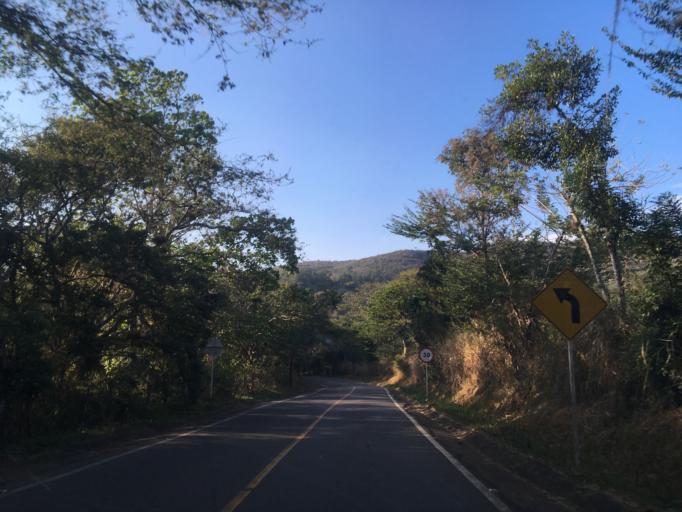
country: CO
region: Santander
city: Barichara
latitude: 6.6375
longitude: -73.2025
